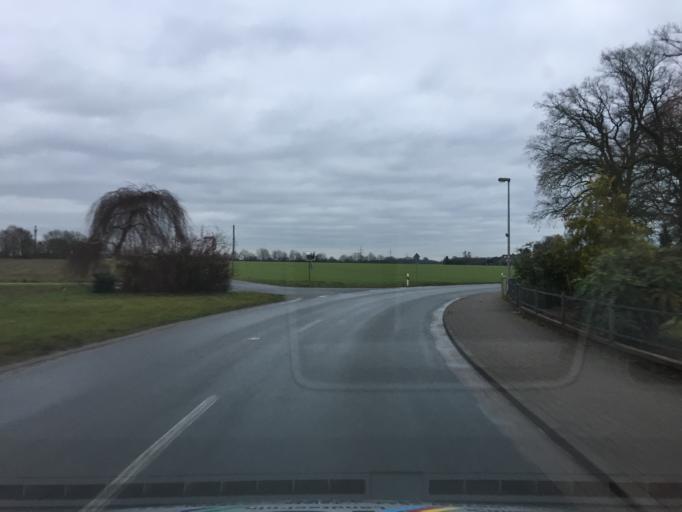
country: DE
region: Lower Saxony
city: Borstel
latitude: 52.6657
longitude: 8.9751
